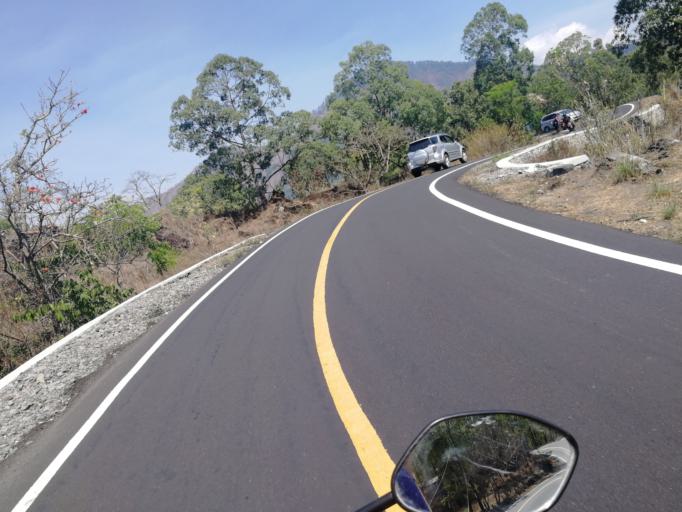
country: ID
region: Bali
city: Banjar Kedisan
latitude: -8.2636
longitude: 115.3899
